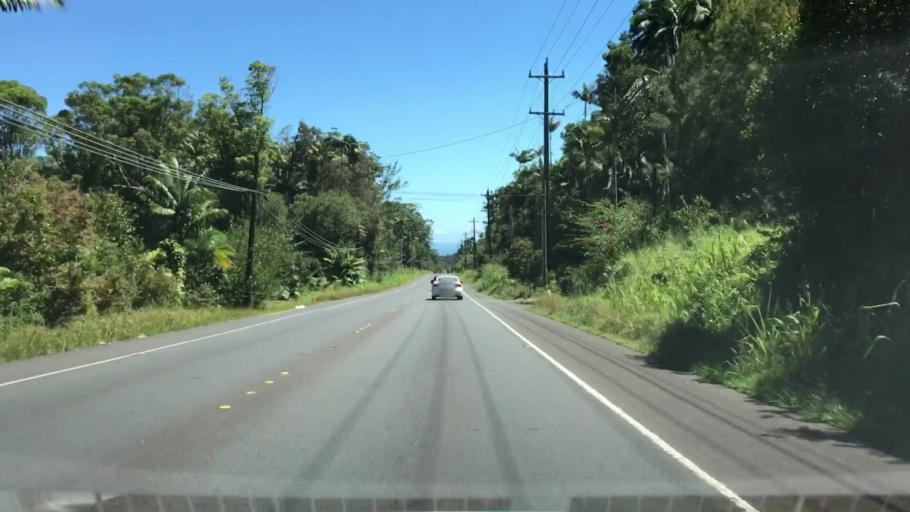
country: US
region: Hawaii
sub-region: Hawaii County
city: Mountain View
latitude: 19.5318
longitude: -155.1302
